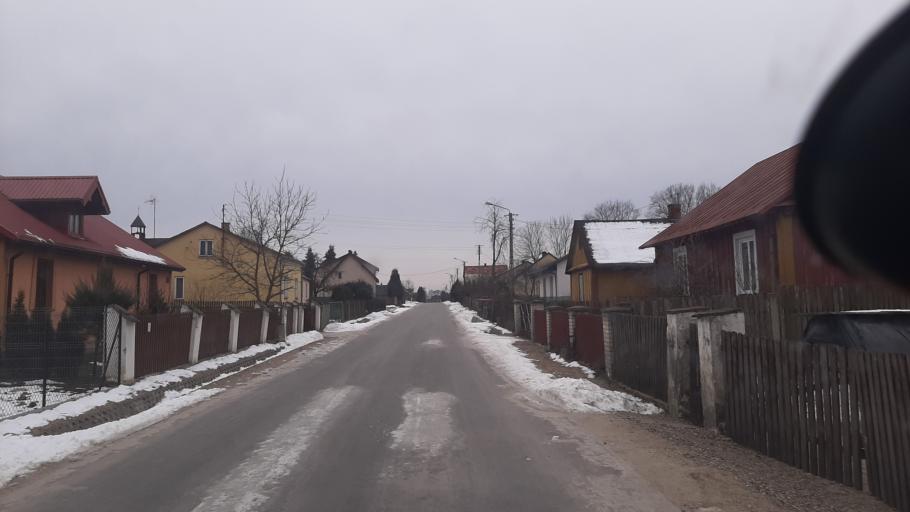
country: PL
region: Lublin Voivodeship
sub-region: Powiat lubartowski
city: Kamionka
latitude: 51.5172
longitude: 22.4741
